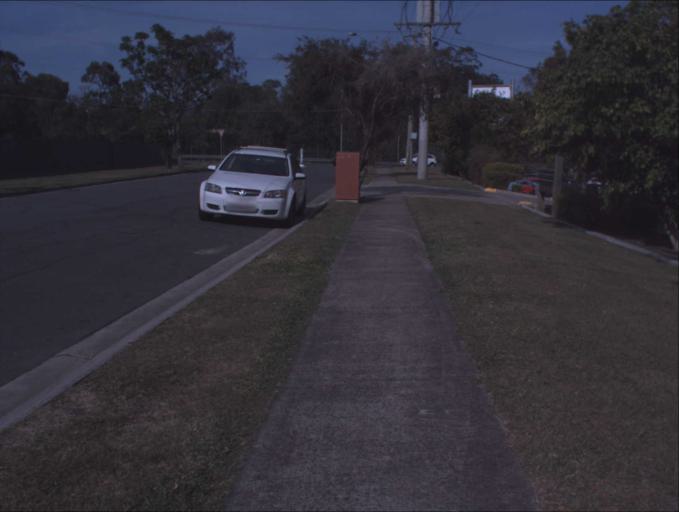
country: AU
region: Queensland
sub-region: Logan
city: Slacks Creek
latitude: -27.6516
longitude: 153.1584
